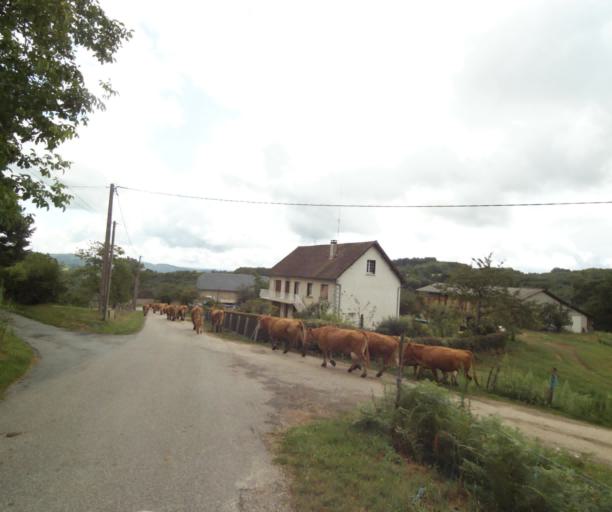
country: FR
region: Limousin
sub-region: Departement de la Correze
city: Sainte-Fortunade
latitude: 45.1666
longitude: 1.8184
